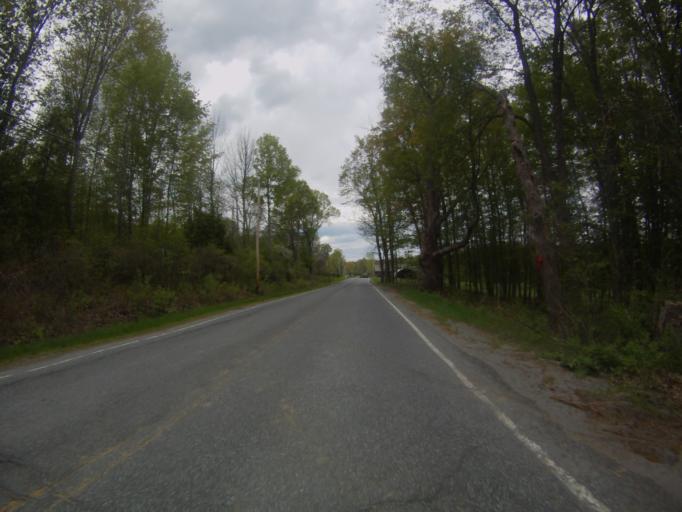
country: US
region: New York
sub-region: Essex County
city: Port Henry
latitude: 44.0311
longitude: -73.5022
